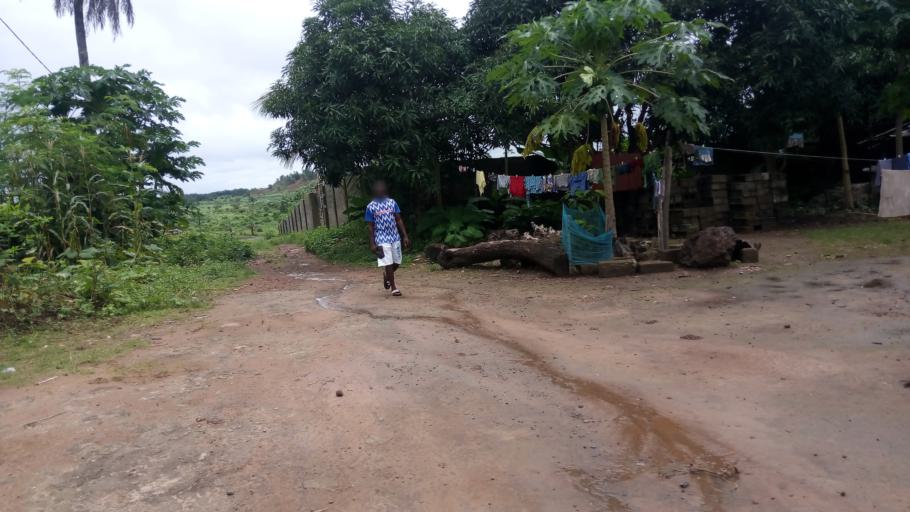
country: SL
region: Northern Province
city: Lunsar
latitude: 8.6929
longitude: -12.5272
